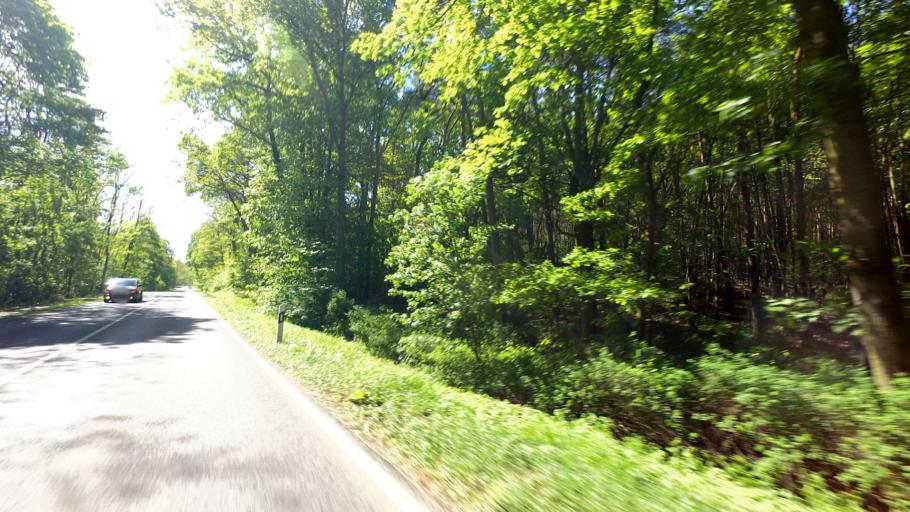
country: DE
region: Brandenburg
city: Michendorf
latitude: 52.3512
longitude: 13.0441
